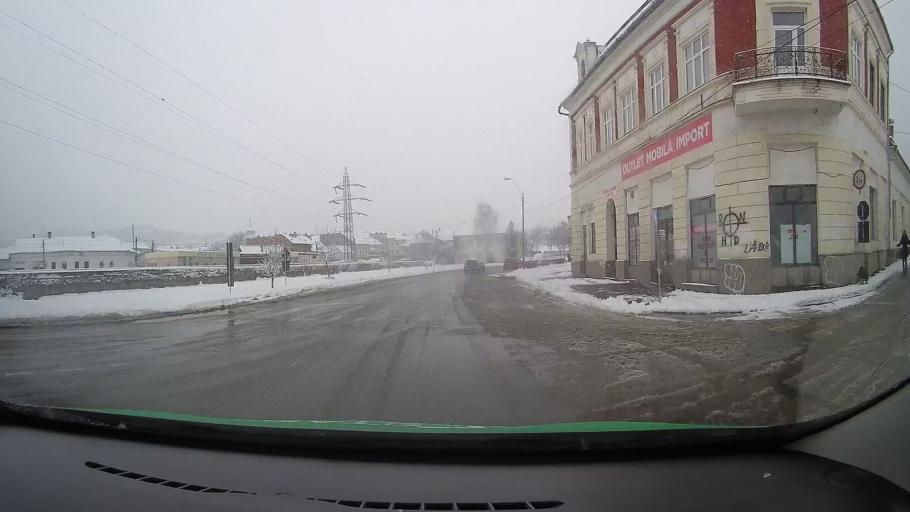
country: RO
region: Hunedoara
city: Hunedoara
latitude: 45.7507
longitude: 22.8937
